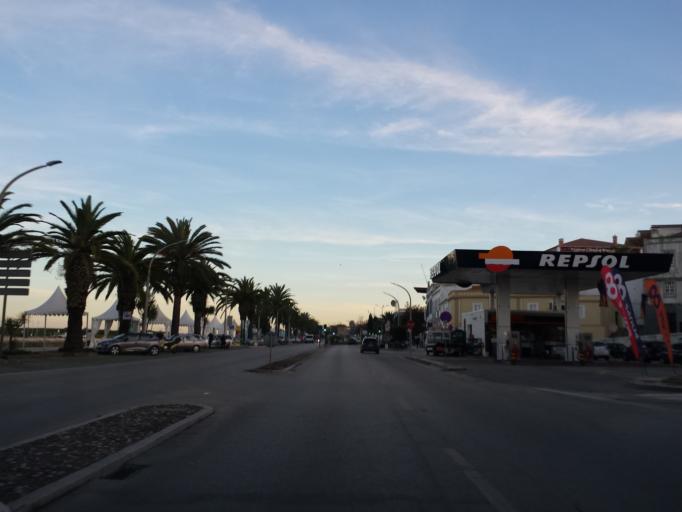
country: PT
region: Faro
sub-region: Lagos
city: Lagos
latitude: 37.1052
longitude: -8.6736
